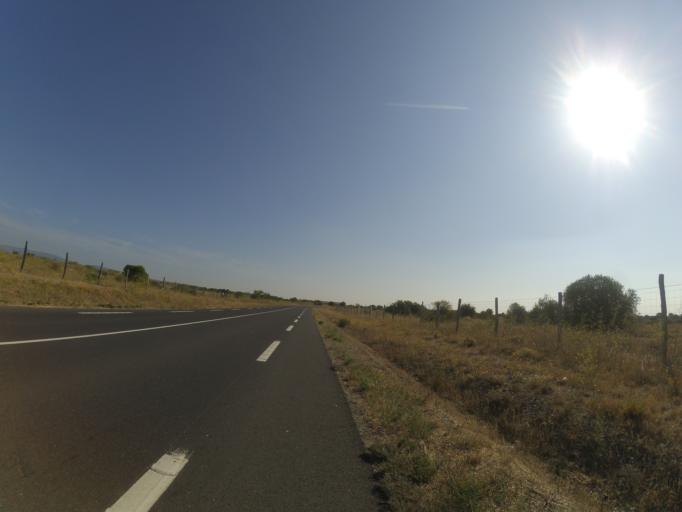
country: FR
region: Languedoc-Roussillon
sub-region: Departement des Pyrenees-Orientales
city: Rivesaltes
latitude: 42.7969
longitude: 2.8599
